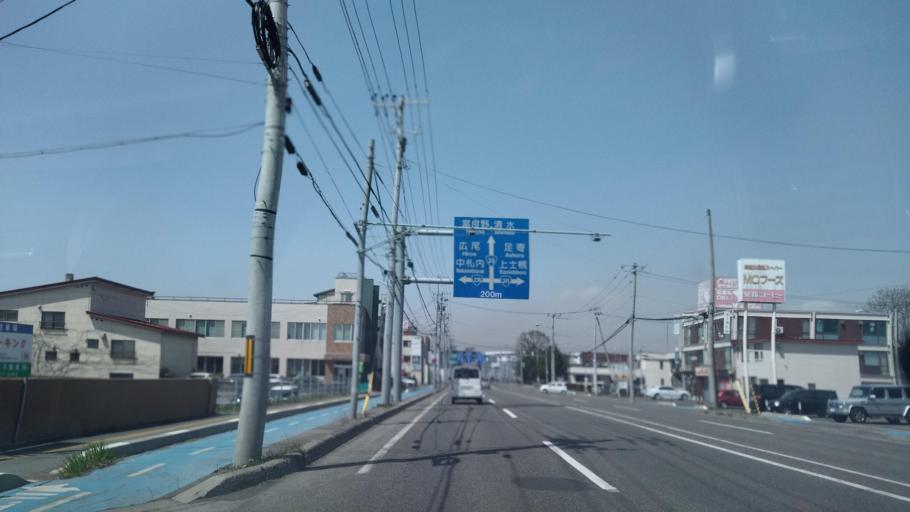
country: JP
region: Hokkaido
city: Obihiro
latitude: 42.9311
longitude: 143.2071
